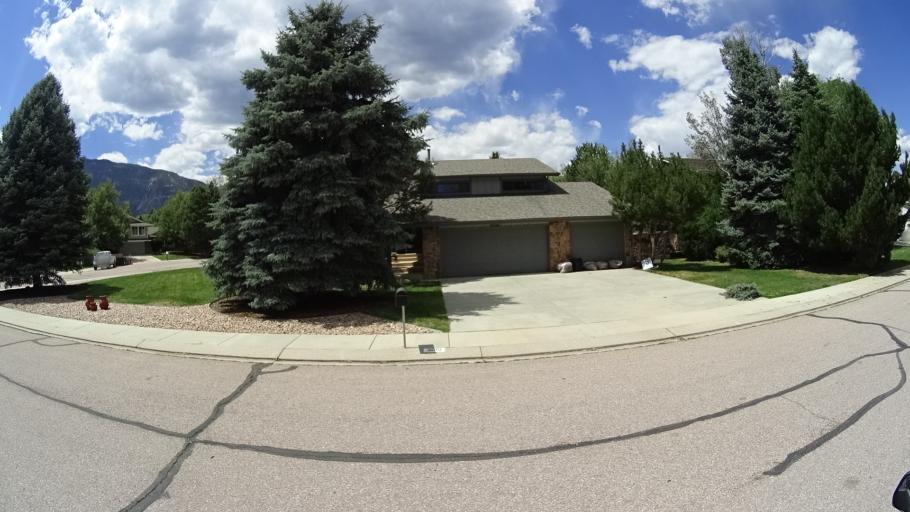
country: US
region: Colorado
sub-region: El Paso County
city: Colorado Springs
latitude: 38.7903
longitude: -104.8328
